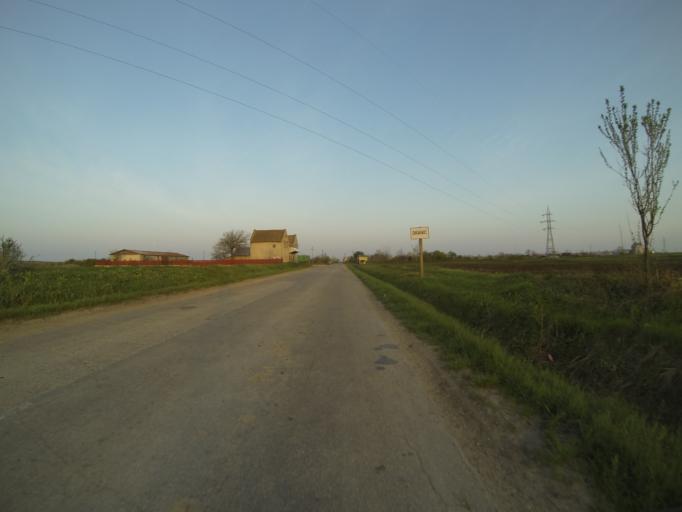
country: RO
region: Dolj
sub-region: Comuna Dranicu
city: Dranic
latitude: 44.0593
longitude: 23.8281
